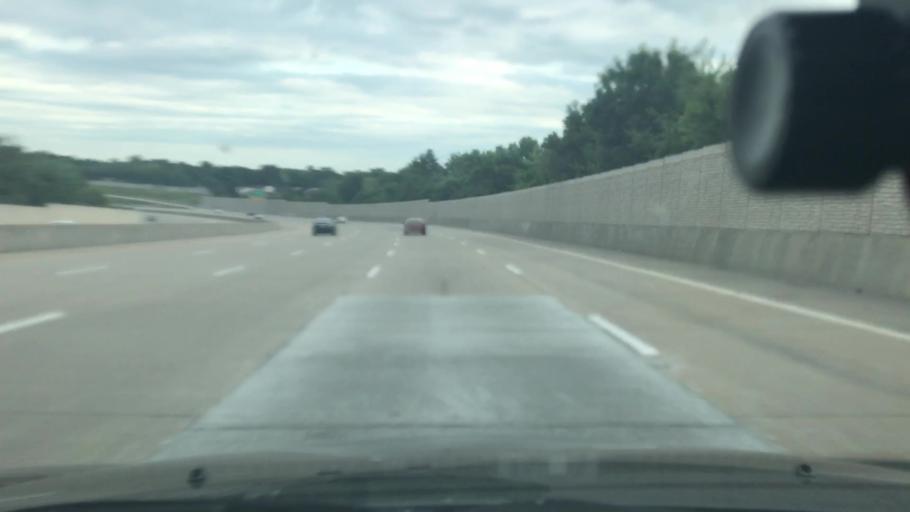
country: US
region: Missouri
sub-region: Saint Louis County
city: Maryland Heights
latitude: 38.6992
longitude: -90.4714
